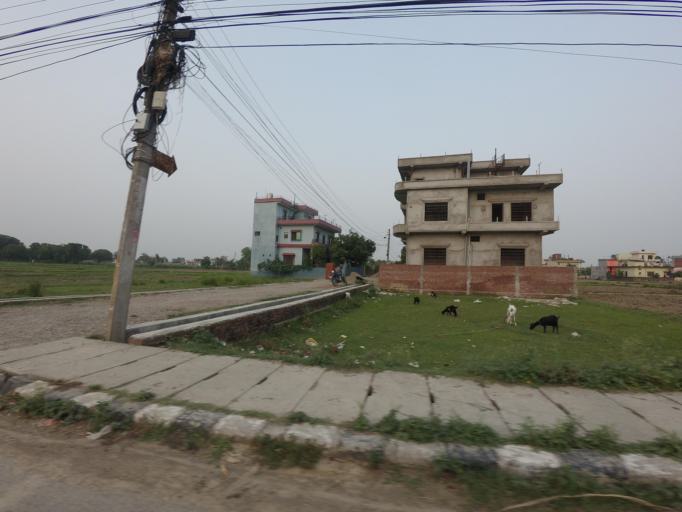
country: NP
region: Western Region
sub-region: Lumbini Zone
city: Bhairahawa
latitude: 27.5139
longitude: 83.4641
